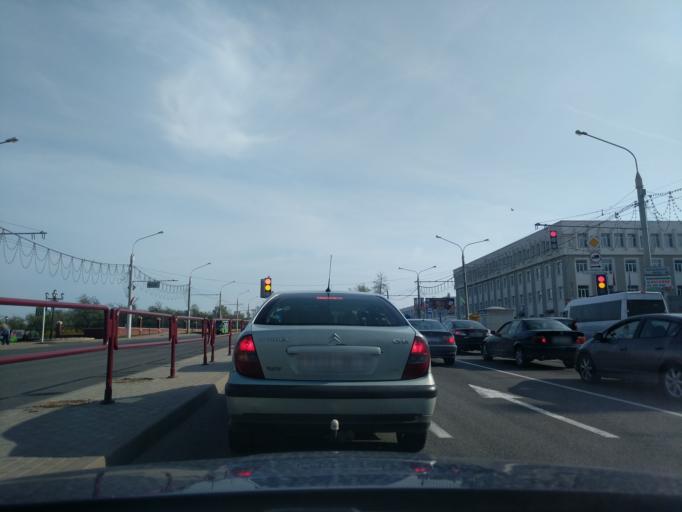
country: BY
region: Minsk
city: Minsk
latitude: 53.8601
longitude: 27.5721
